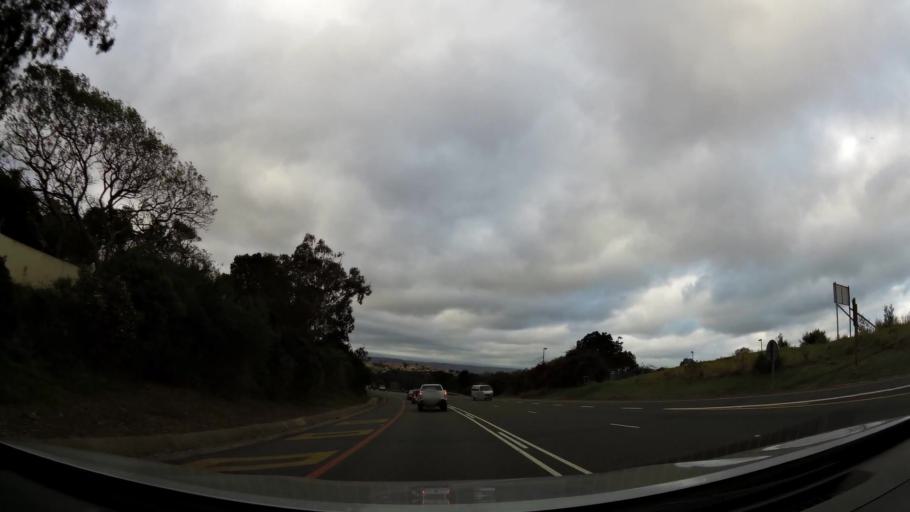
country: ZA
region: Western Cape
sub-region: Eden District Municipality
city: Plettenberg Bay
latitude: -34.0482
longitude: 23.3600
